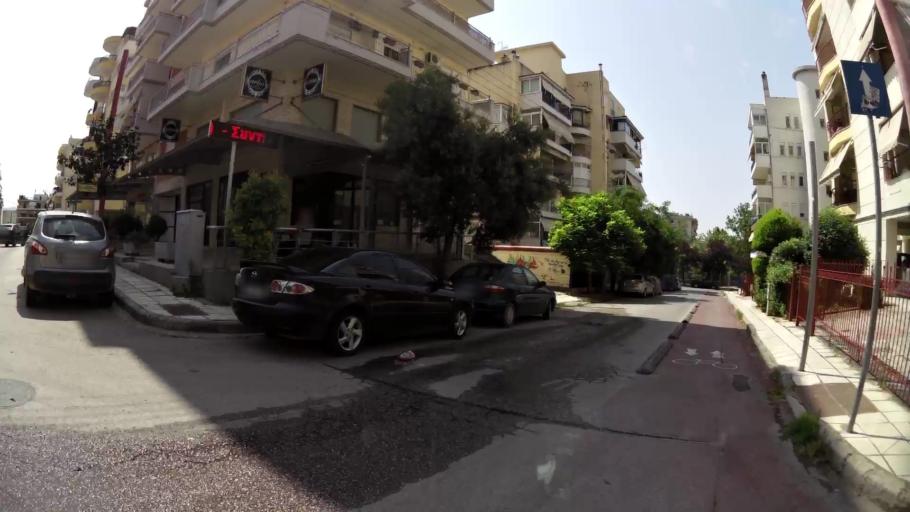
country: GR
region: Central Macedonia
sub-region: Nomos Thessalonikis
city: Evosmos
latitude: 40.6757
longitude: 22.9203
